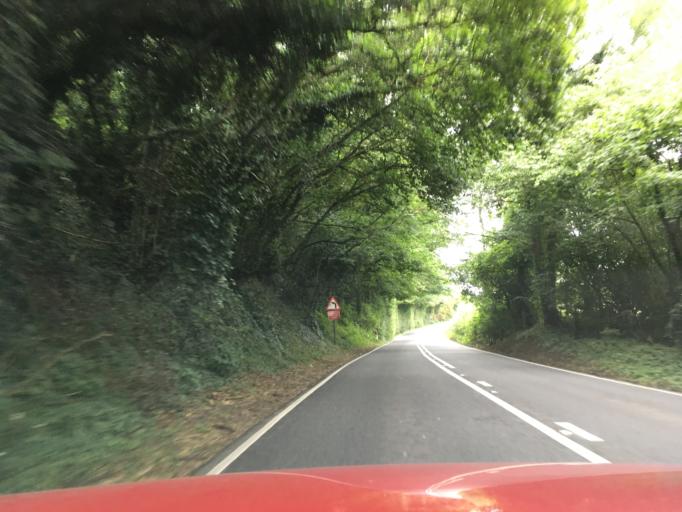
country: GB
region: England
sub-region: Hampshire
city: Petersfield
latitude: 51.0095
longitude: -0.9860
